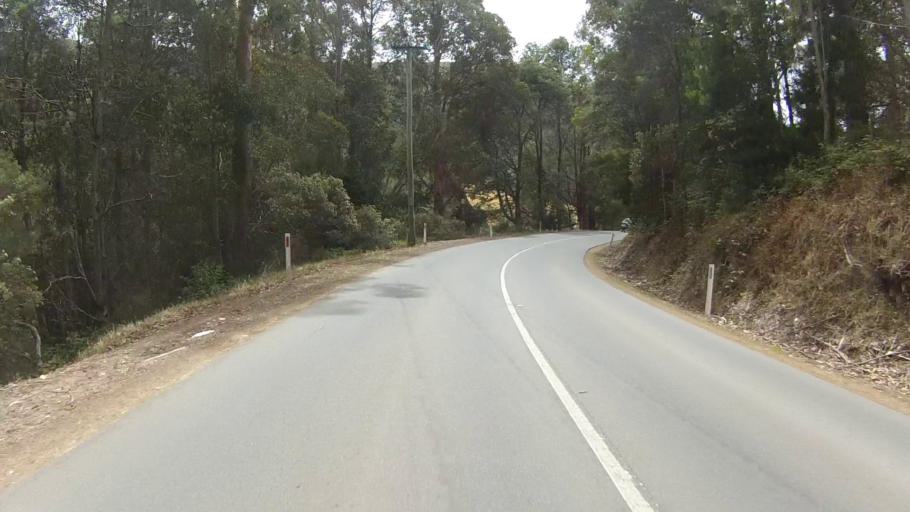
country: AU
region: Tasmania
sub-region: Kingborough
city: Kettering
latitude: -43.1076
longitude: 147.2023
